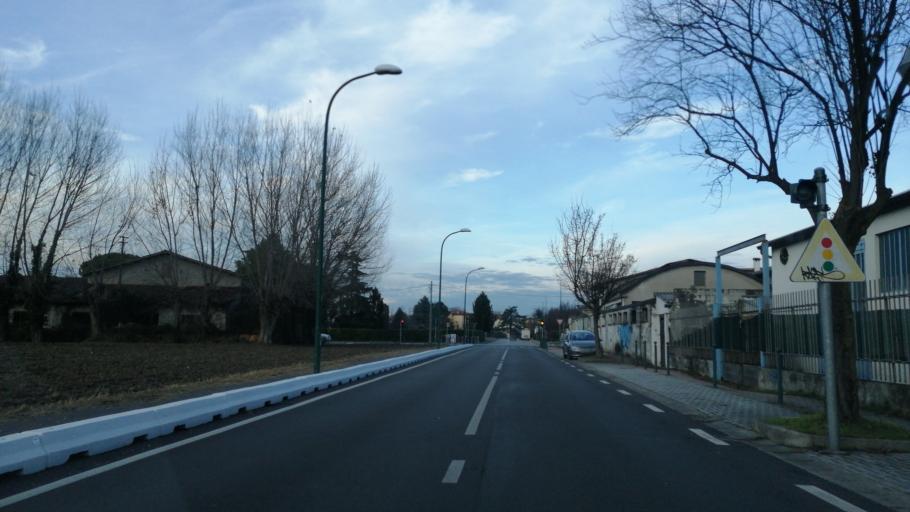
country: IT
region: Veneto
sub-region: Provincia di Venezia
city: Zelarino
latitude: 45.4920
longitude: 12.2108
